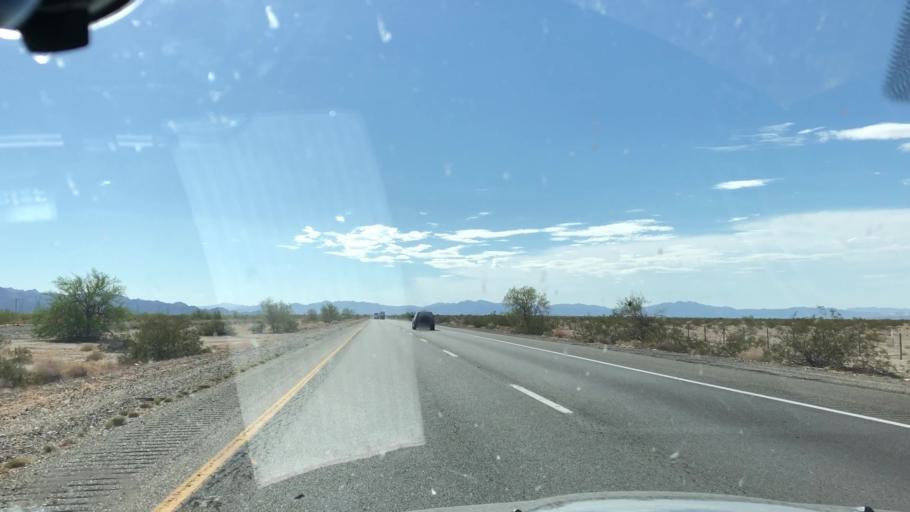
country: US
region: California
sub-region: Riverside County
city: Mesa Verde
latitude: 33.6664
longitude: -115.1887
